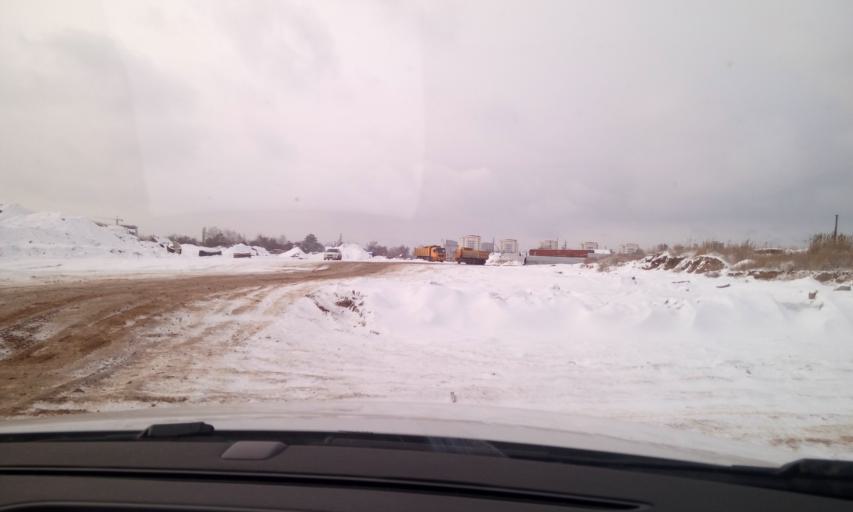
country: KZ
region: Astana Qalasy
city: Astana
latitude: 51.1171
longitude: 71.5182
